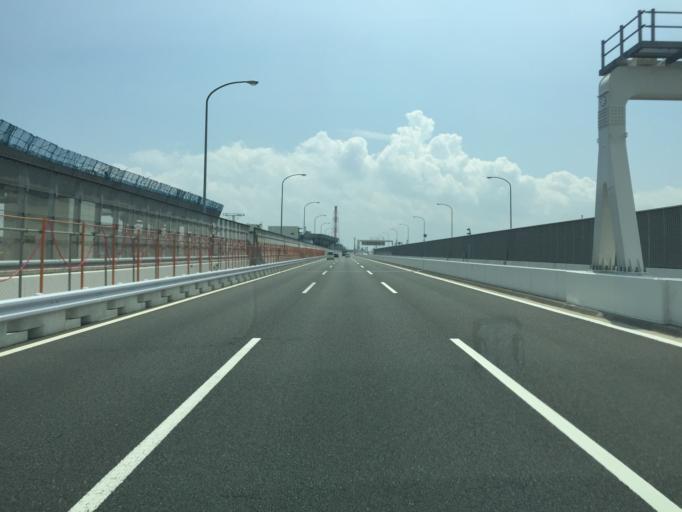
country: JP
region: Kanagawa
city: Yokohama
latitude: 35.4231
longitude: 139.6708
